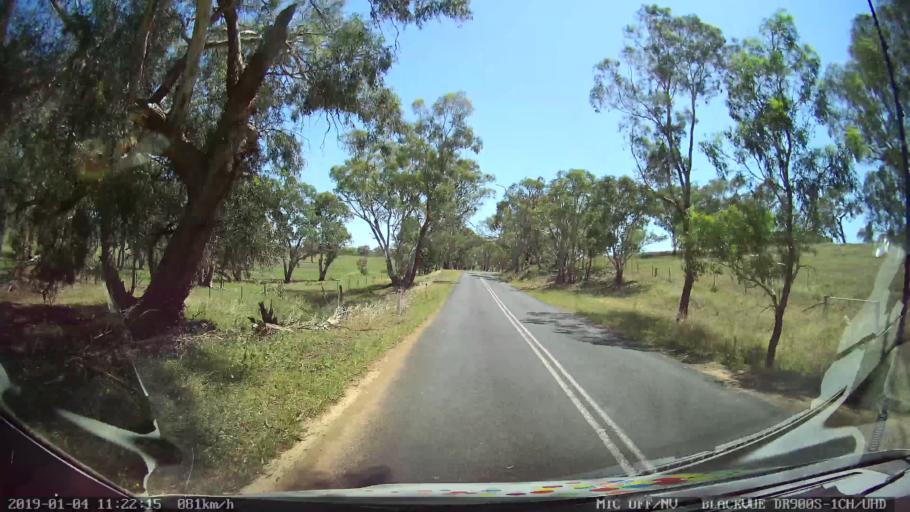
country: AU
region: New South Wales
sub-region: Cabonne
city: Molong
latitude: -33.1474
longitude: 148.7195
